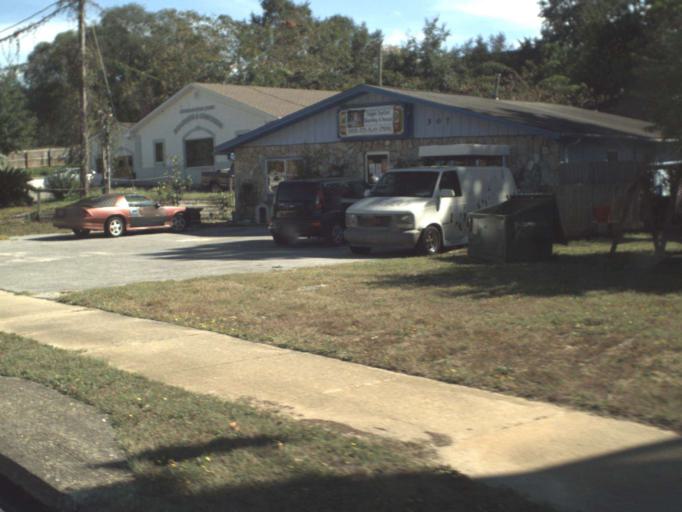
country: US
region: Florida
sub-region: Okaloosa County
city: Niceville
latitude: 30.5200
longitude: -86.4842
